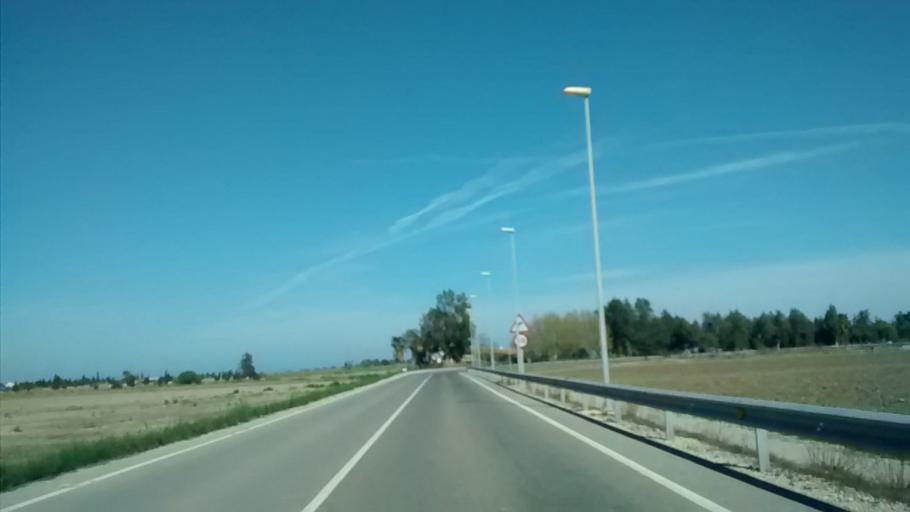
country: ES
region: Catalonia
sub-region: Provincia de Tarragona
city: Deltebre
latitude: 40.7150
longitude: 0.8309
